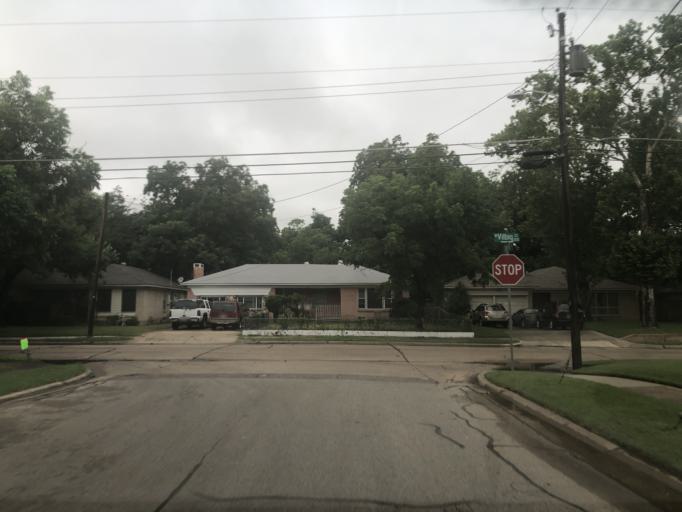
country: US
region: Texas
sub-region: Dallas County
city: Irving
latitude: 32.7974
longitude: -96.9488
